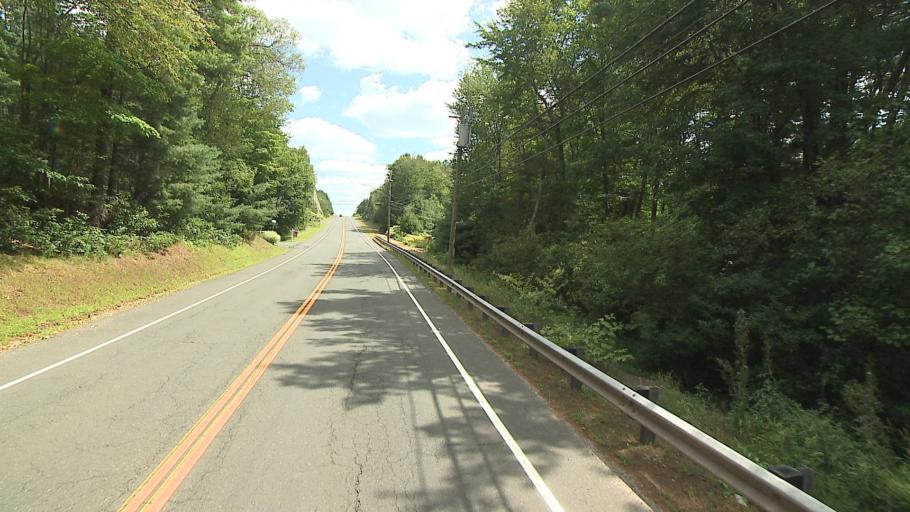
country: US
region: Connecticut
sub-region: Tolland County
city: Crystal Lake
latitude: 41.9313
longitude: -72.3673
